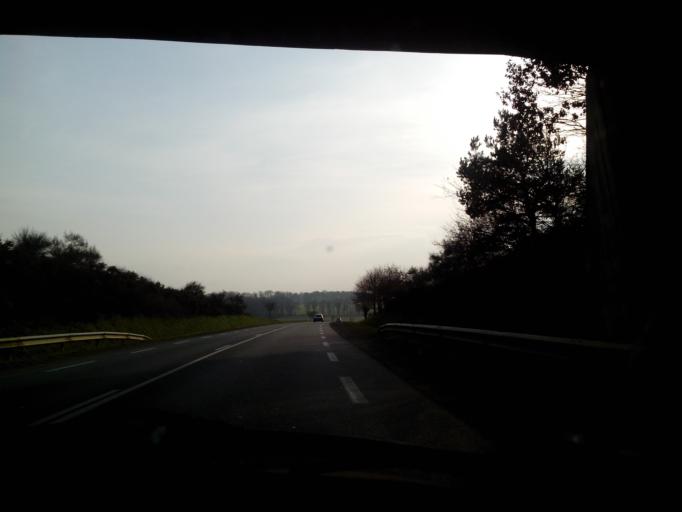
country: FR
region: Brittany
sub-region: Departement du Morbihan
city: Loyat
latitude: 47.9671
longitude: -2.3836
